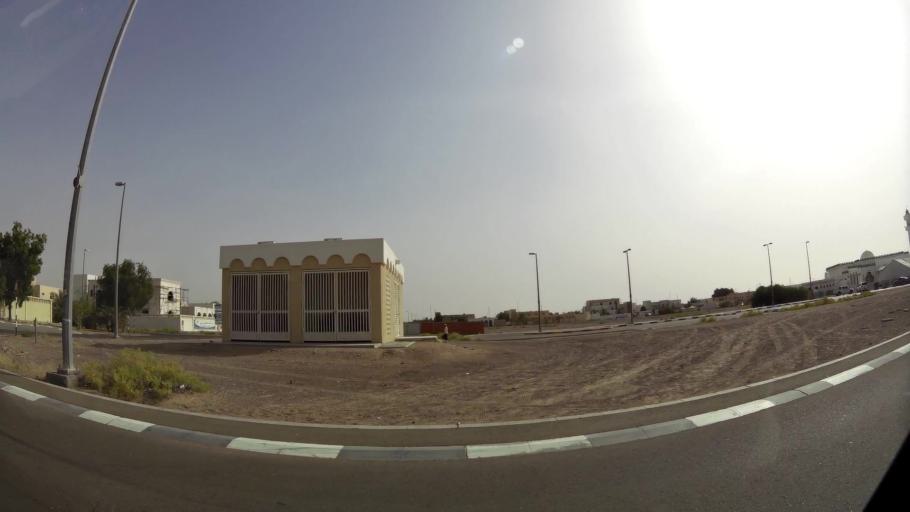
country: AE
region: Abu Dhabi
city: Al Ain
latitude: 24.2078
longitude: 55.5944
